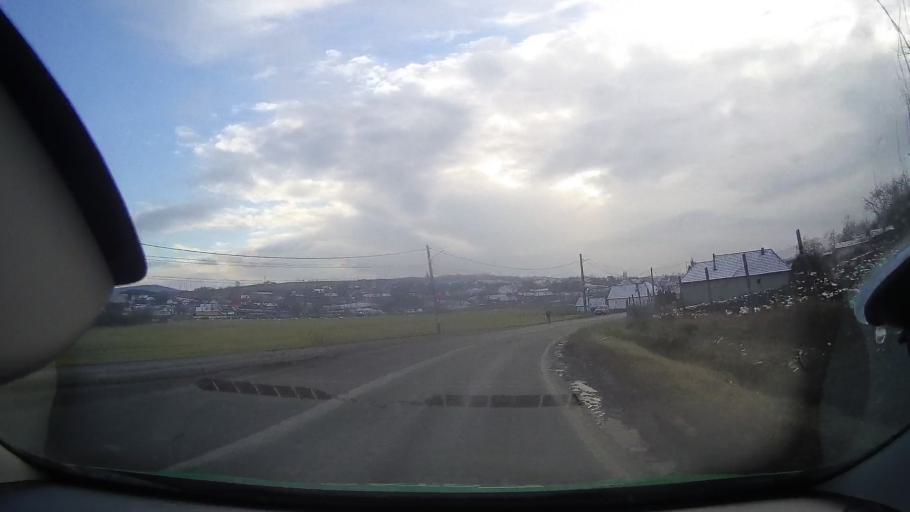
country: RO
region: Mures
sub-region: Comuna Cucerdea
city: Cucerdea
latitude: 46.4092
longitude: 24.2683
